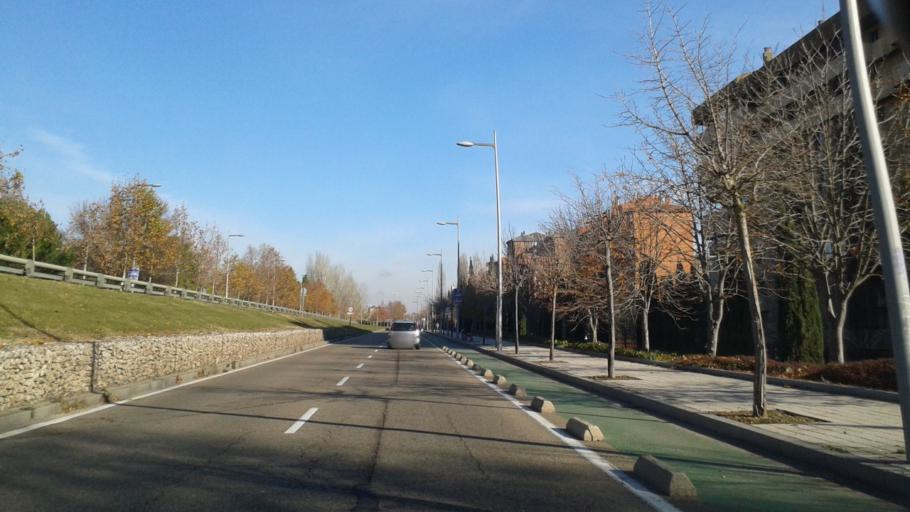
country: ES
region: Castille and Leon
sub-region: Provincia de Valladolid
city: Valladolid
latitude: 41.6303
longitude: -4.7534
